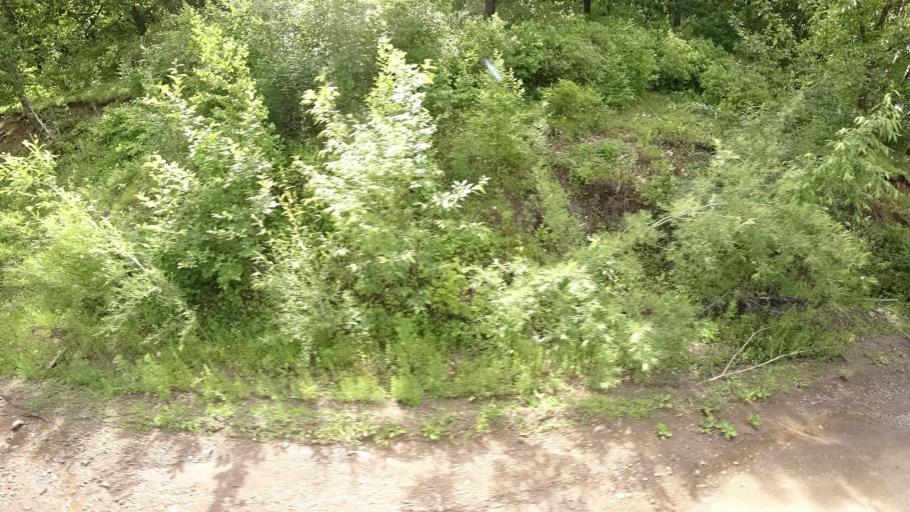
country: RU
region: Khabarovsk Krai
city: Litovko
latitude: 49.3658
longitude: 135.1832
